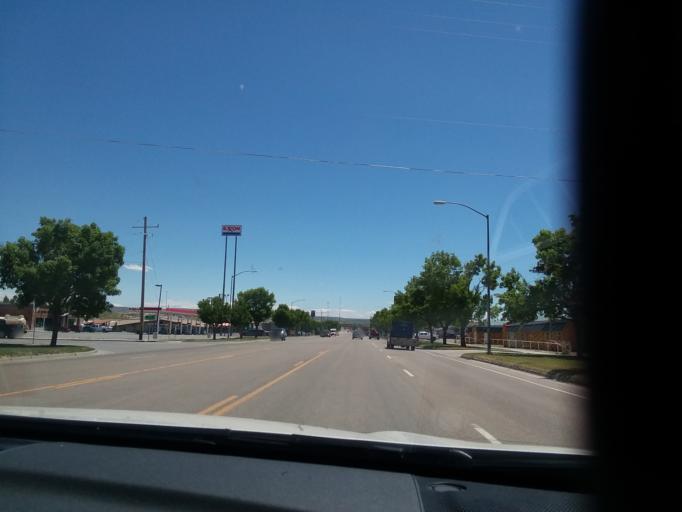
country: US
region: Wyoming
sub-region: Sweetwater County
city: Rock Springs
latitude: 41.6147
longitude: -109.2314
